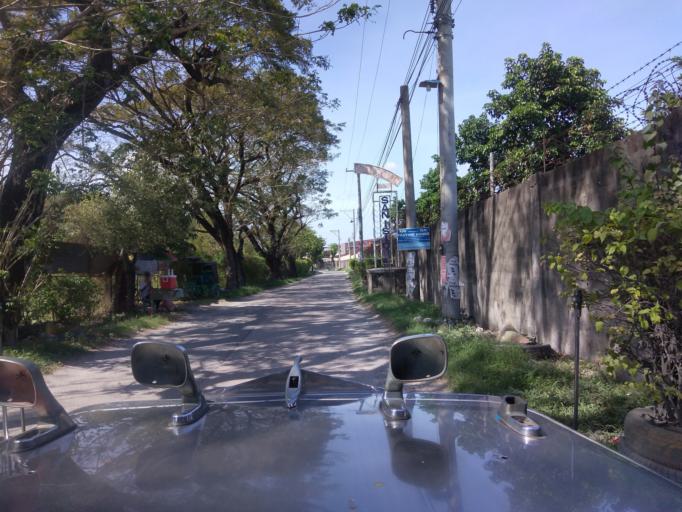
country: PH
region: Central Luzon
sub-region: Province of Pampanga
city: Magliman
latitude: 15.0392
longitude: 120.6604
